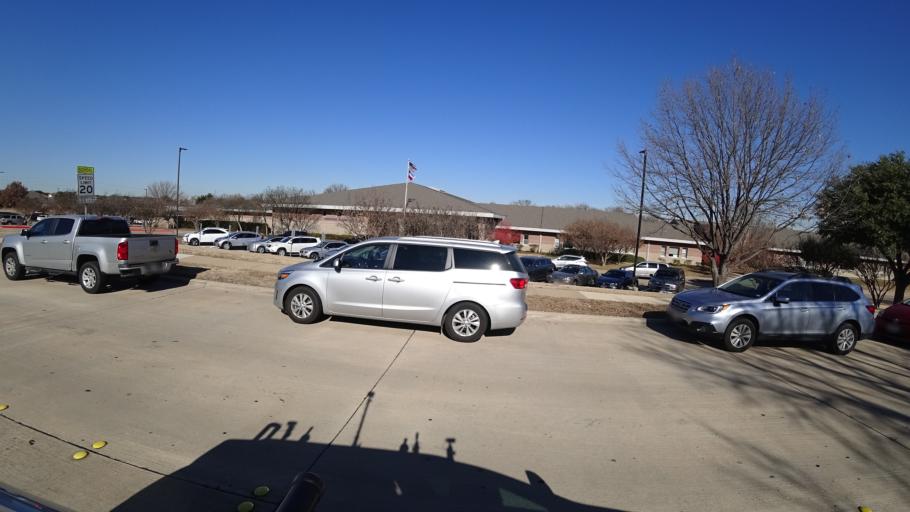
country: US
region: Texas
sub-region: Denton County
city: Lewisville
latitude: 33.0133
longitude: -97.0067
